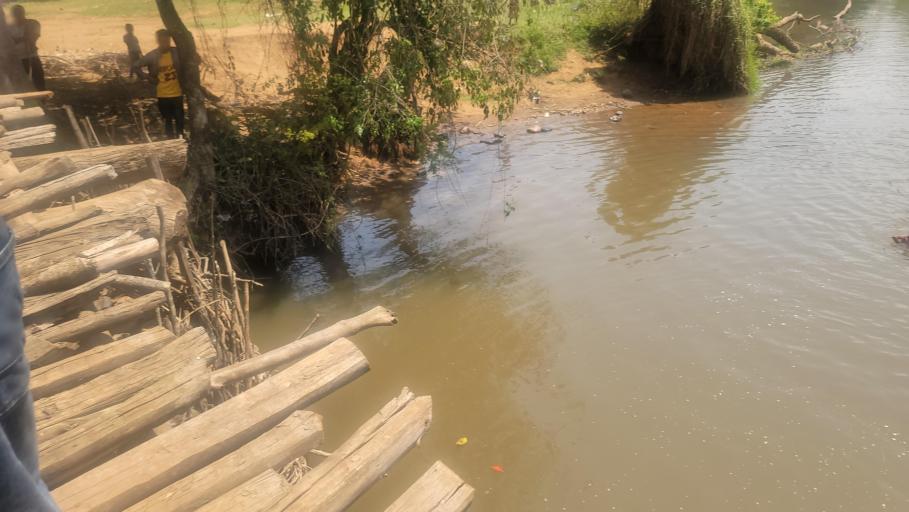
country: ET
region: Southern Nations, Nationalities, and People's Region
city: Bonga
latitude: 7.4963
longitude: 36.2982
